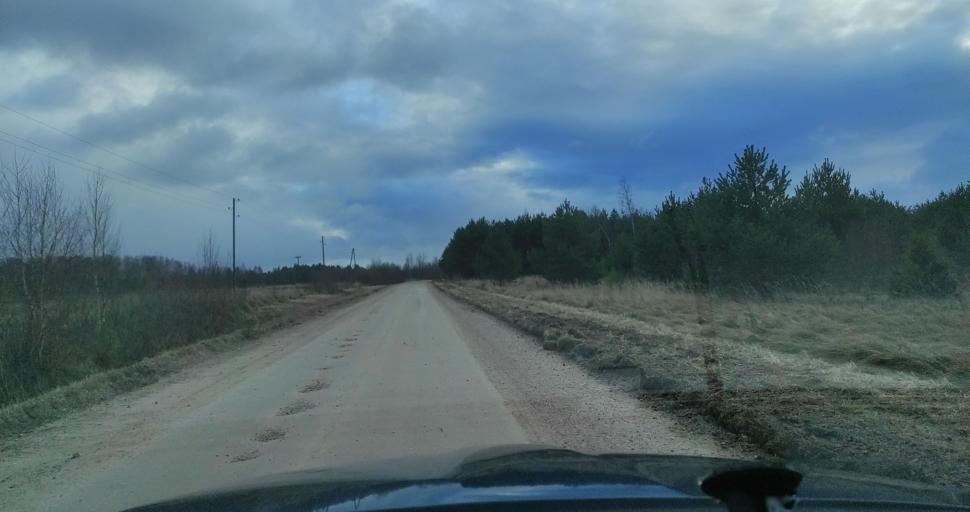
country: LV
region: Pavilostas
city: Pavilosta
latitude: 56.7737
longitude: 21.0739
